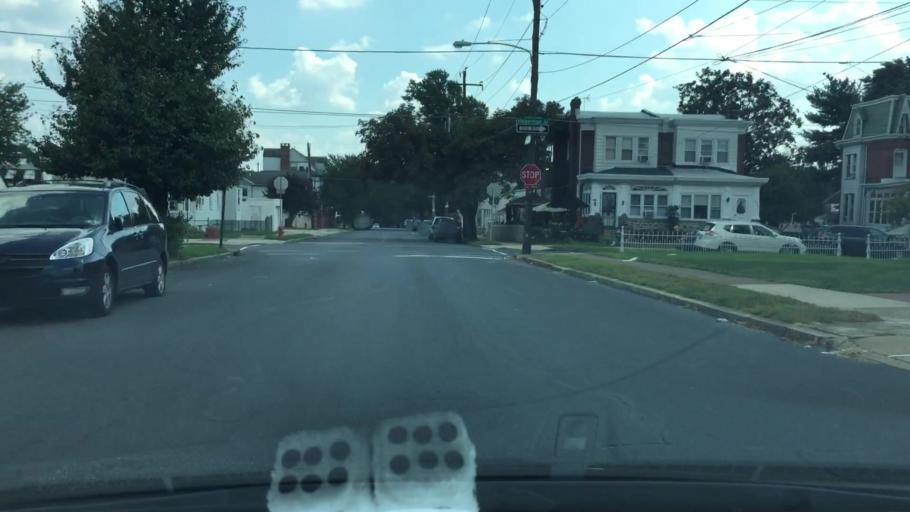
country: US
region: New Jersey
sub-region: Burlington County
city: Palmyra
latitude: 40.0264
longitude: -75.0404
